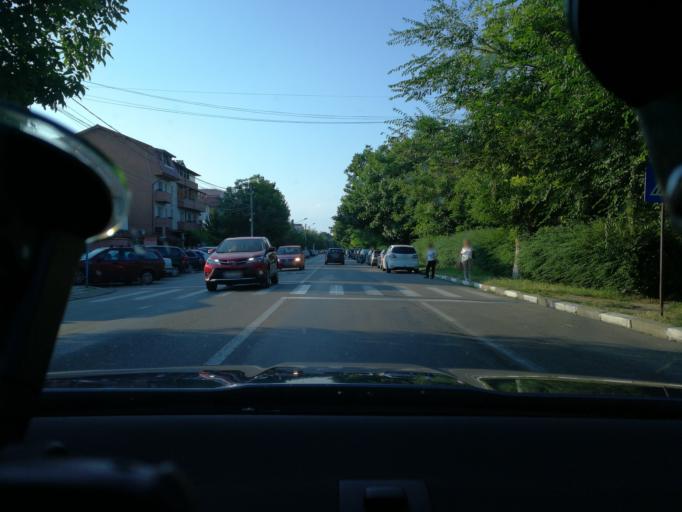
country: RO
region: Constanta
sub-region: Oras Eforie
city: Eforie Nord
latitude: 44.0721
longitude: 28.6289
